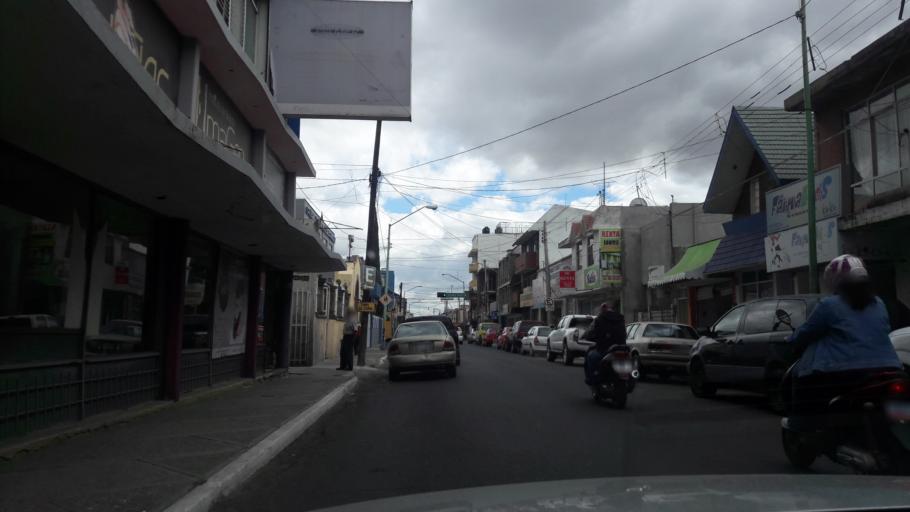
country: MX
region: Guanajuato
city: Salamanca
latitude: 20.5693
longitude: -101.1963
